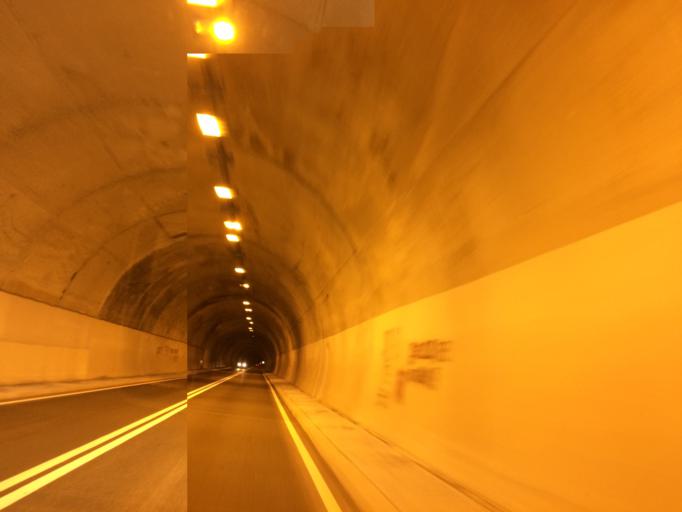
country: ME
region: Opstina Savnik
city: Savnik
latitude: 43.0555
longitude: 19.1014
